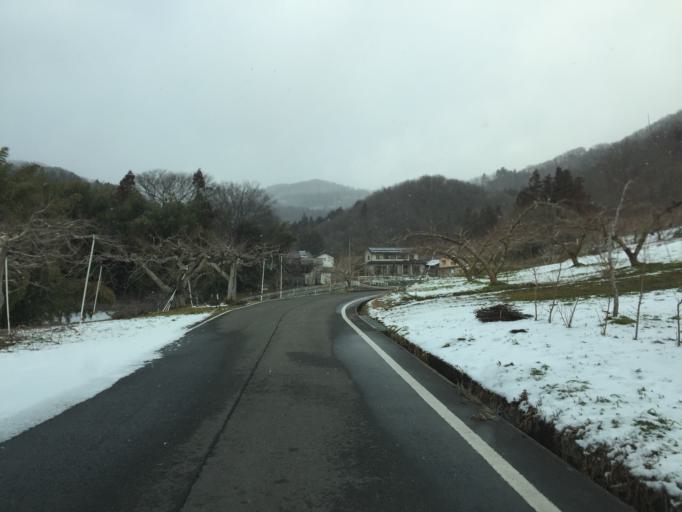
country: JP
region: Fukushima
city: Hobaramachi
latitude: 37.8418
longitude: 140.4663
